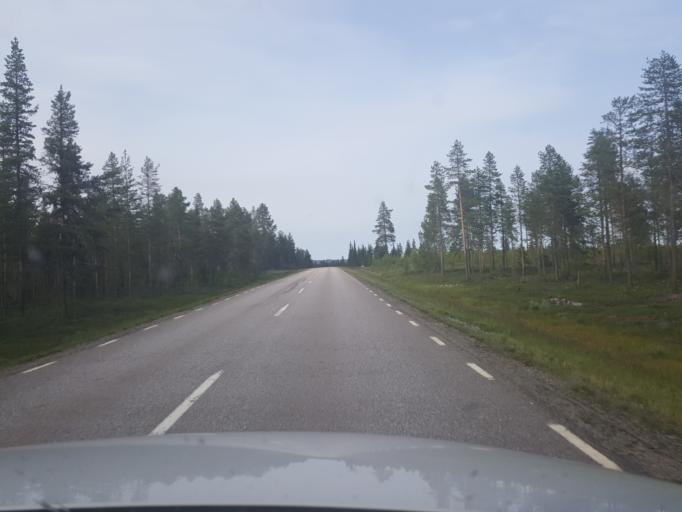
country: SE
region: Norrbotten
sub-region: Arjeplogs Kommun
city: Arjeplog
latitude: 65.7106
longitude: 18.0815
